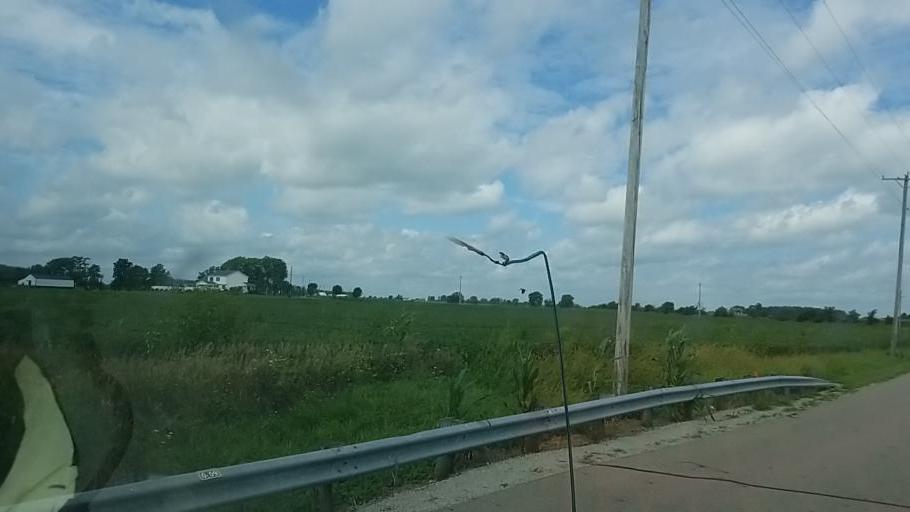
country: US
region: Ohio
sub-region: Fayette County
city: Jeffersonville
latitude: 39.6691
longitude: -83.5754
